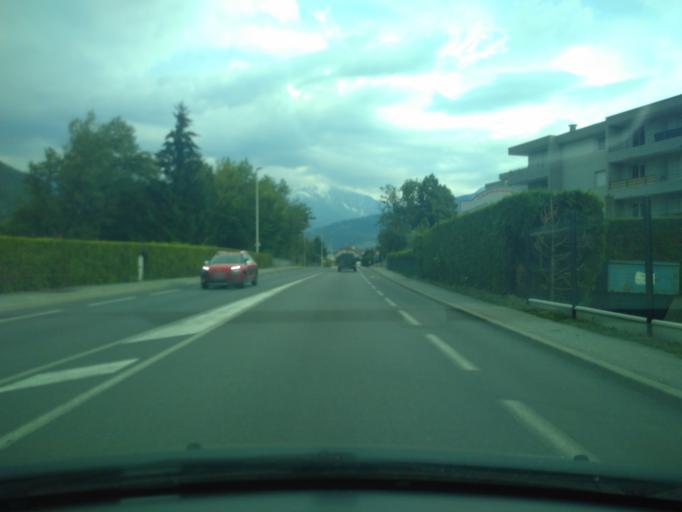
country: FR
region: Rhone-Alpes
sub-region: Departement de la Haute-Savoie
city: Sallanches
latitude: 45.9414
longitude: 6.6388
